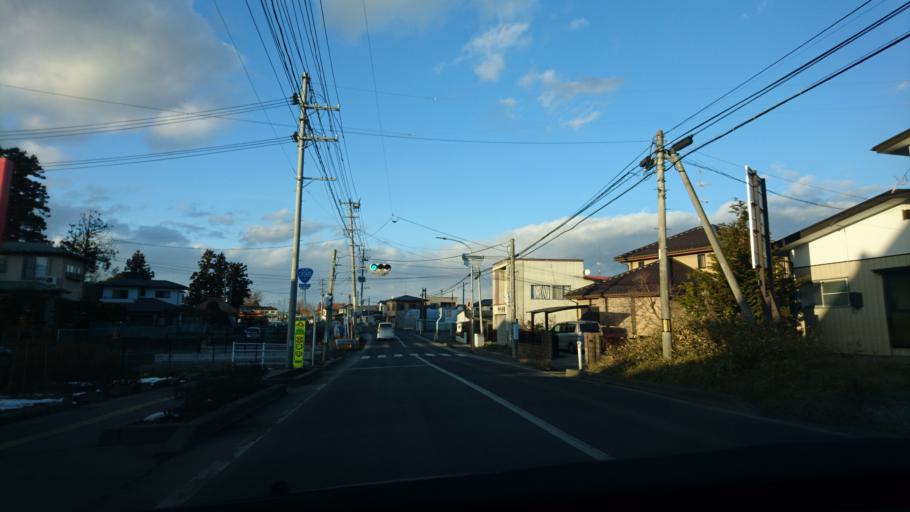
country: JP
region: Miyagi
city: Wakuya
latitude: 38.6957
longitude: 141.1926
